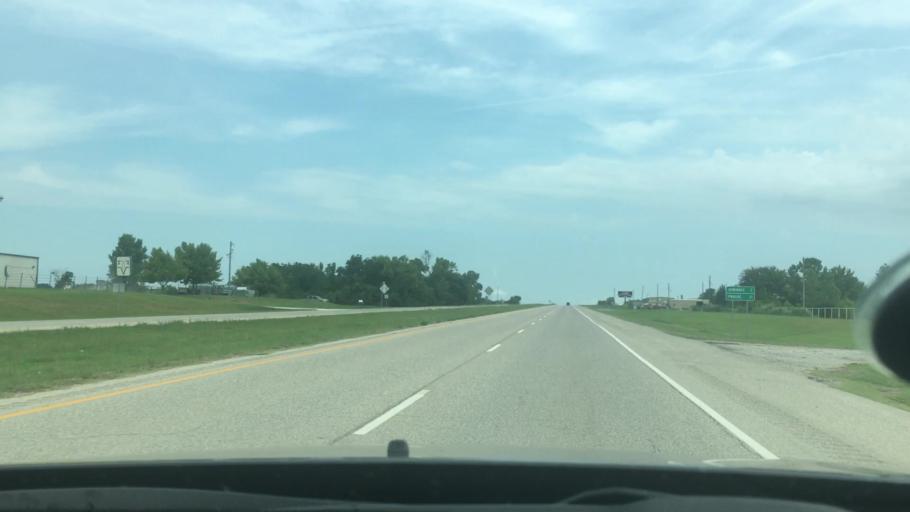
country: US
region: Oklahoma
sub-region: Seminole County
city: Seminole
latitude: 35.1900
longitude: -96.6749
